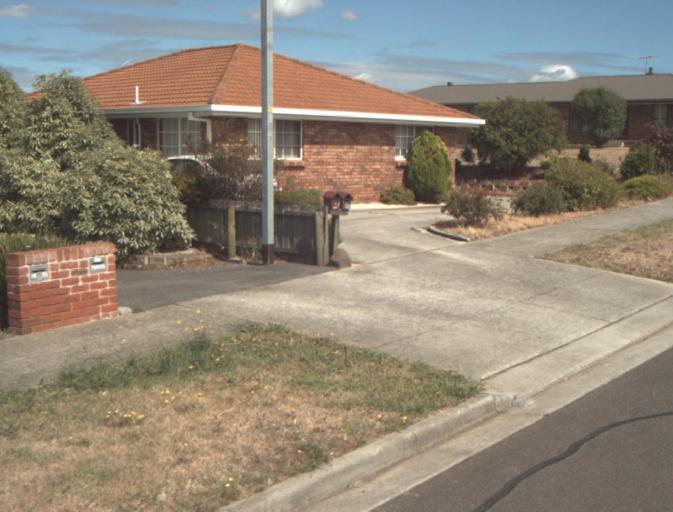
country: AU
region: Tasmania
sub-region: Launceston
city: Mayfield
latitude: -41.3844
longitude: 147.1121
